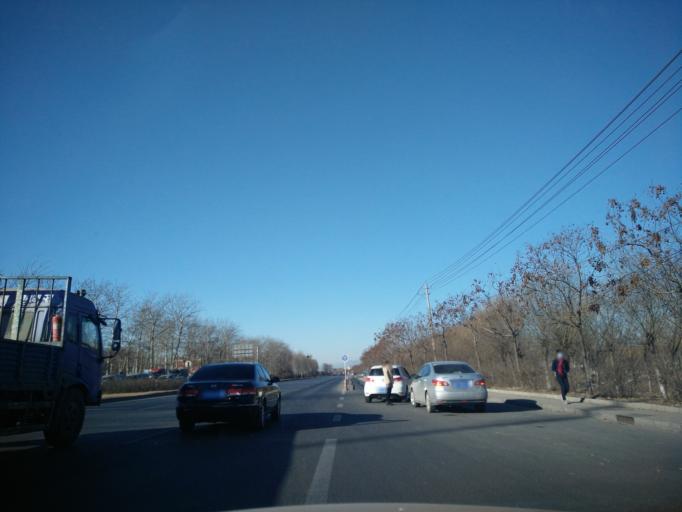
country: CN
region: Beijing
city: Xingfeng
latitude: 39.7207
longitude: 116.3714
